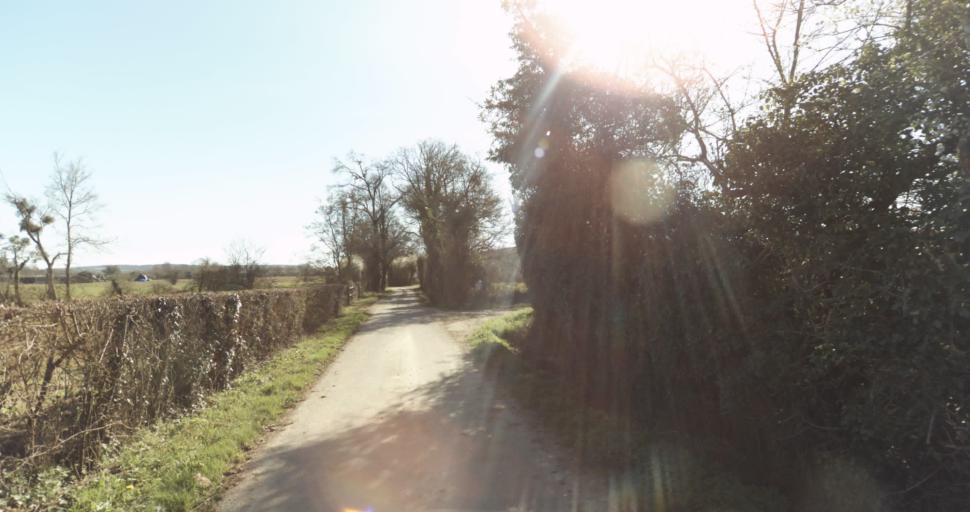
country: FR
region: Lower Normandy
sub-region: Departement du Calvados
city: Saint-Pierre-sur-Dives
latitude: 49.0518
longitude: 0.0561
